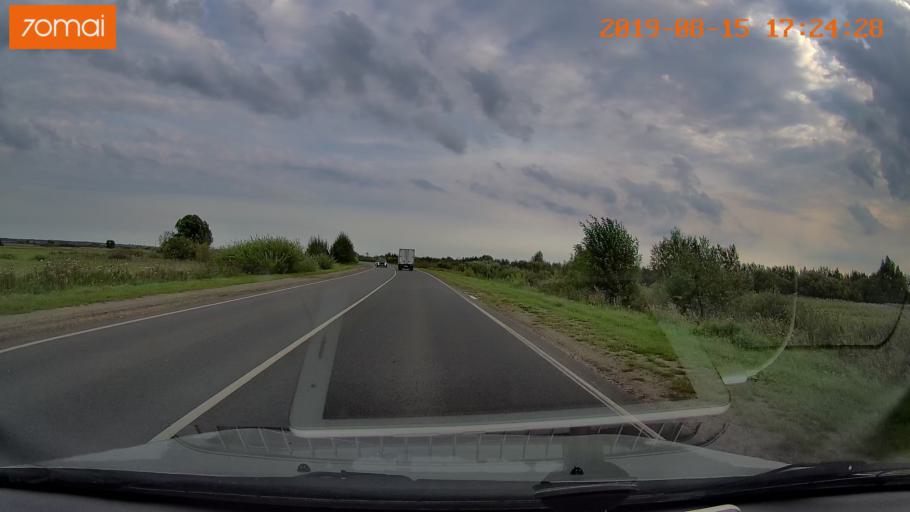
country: RU
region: Moskovskaya
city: Ashitkovo
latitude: 55.3865
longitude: 38.5551
